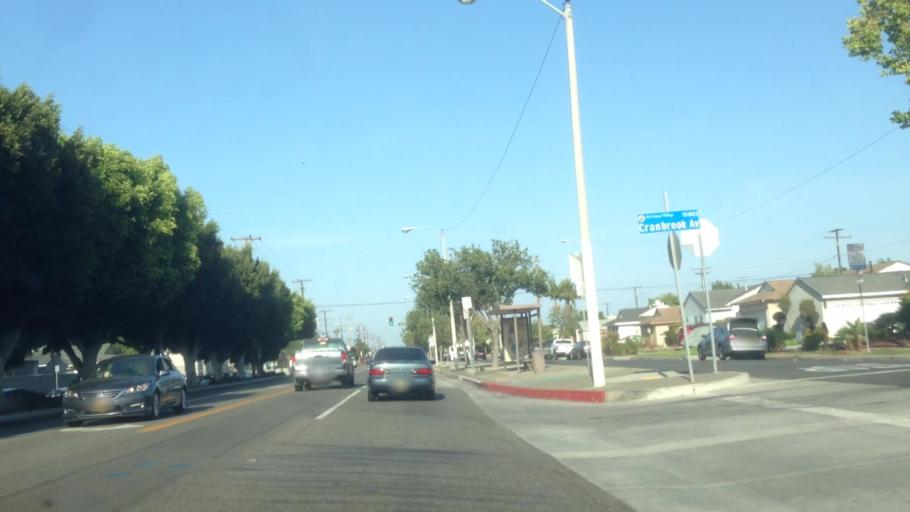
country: US
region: California
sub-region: Los Angeles County
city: Alondra Park
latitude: 33.8946
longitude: -118.3368
